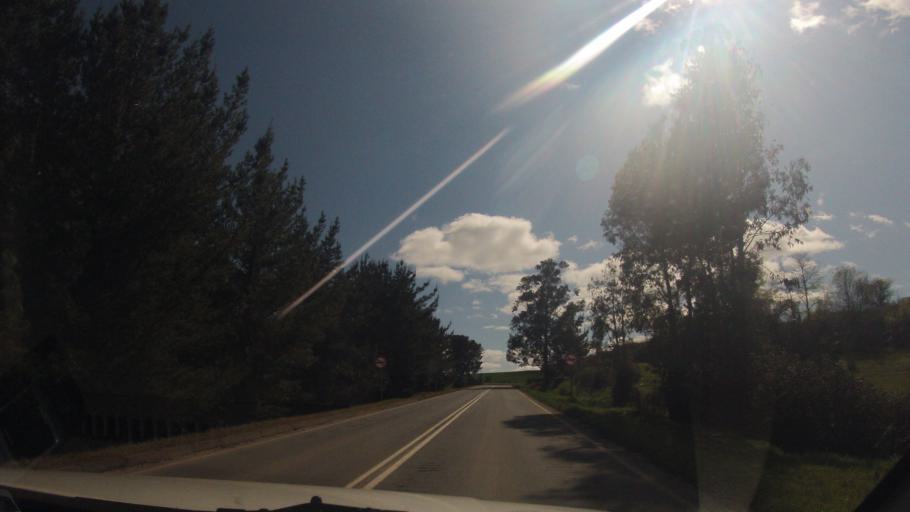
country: CL
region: Araucania
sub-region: Provincia de Malleco
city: Traiguen
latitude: -38.2413
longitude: -72.6894
